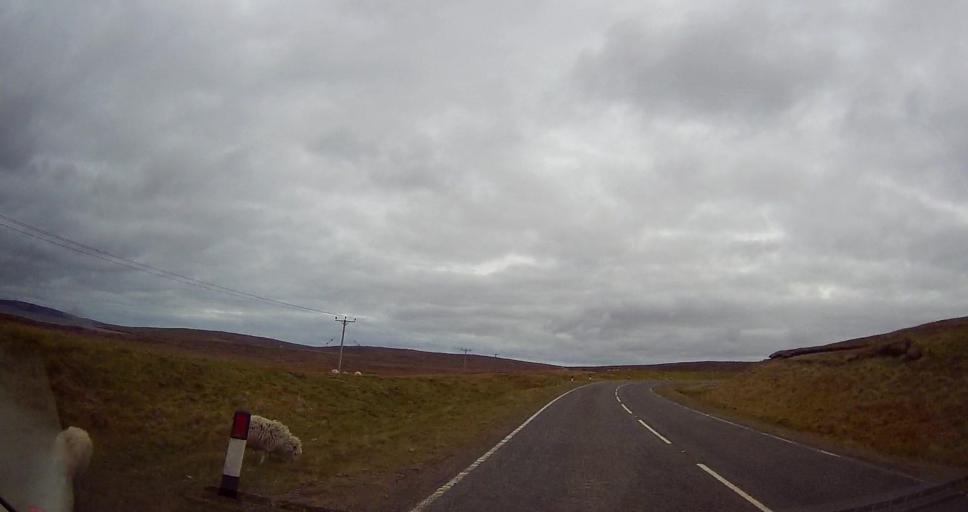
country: GB
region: Scotland
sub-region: Shetland Islands
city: Shetland
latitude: 60.6499
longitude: -1.0666
